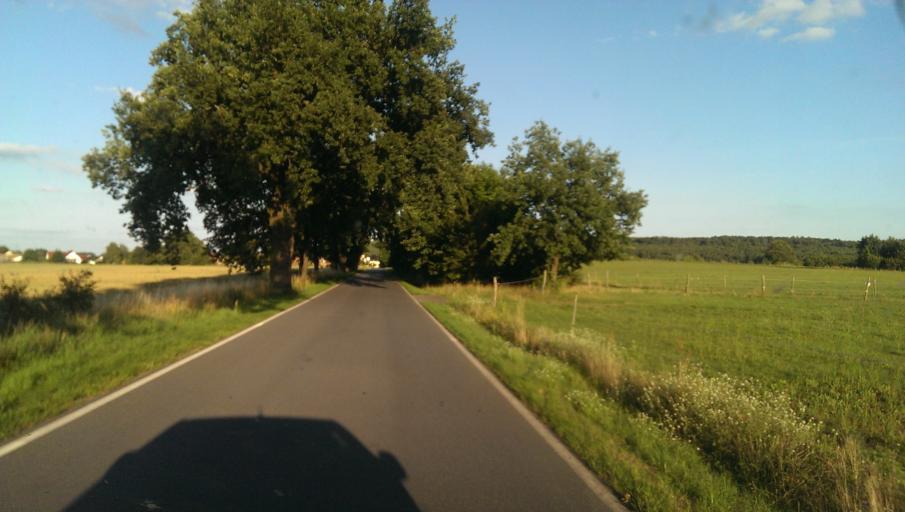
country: DE
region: Brandenburg
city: Trebbin
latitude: 52.2573
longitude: 13.1550
